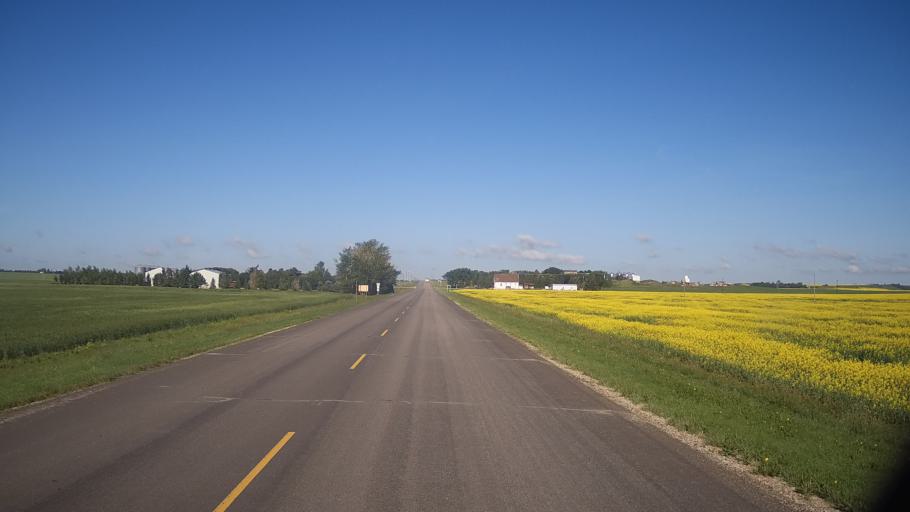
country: CA
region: Saskatchewan
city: Watrous
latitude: 51.6781
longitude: -105.3974
